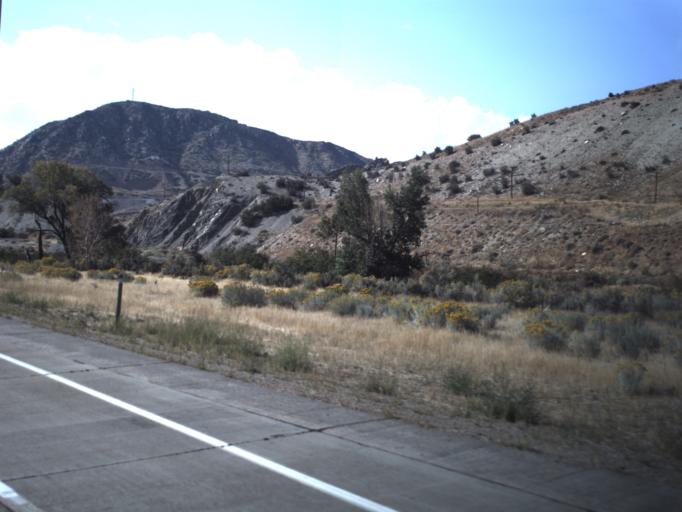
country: US
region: Utah
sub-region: Morgan County
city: Morgan
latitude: 41.0573
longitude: -111.5338
